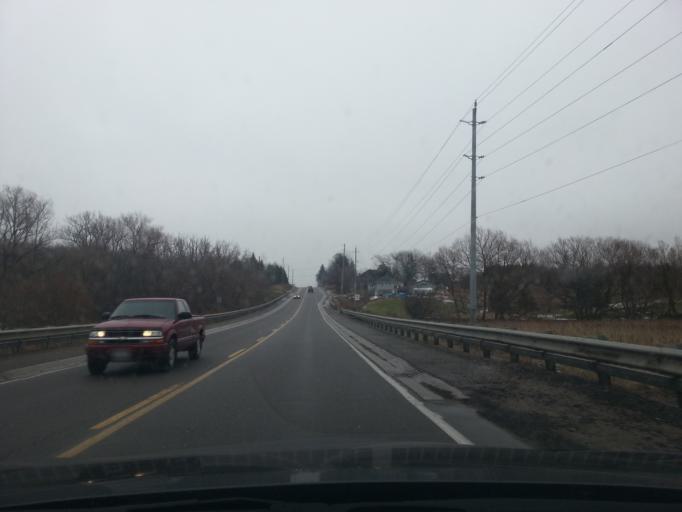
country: CA
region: Ontario
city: Uxbridge
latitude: 44.1037
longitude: -78.9271
